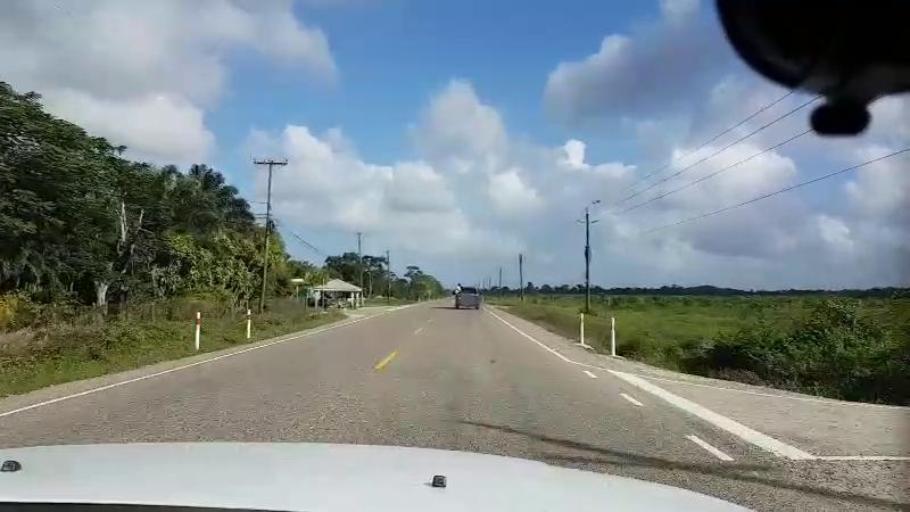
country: BZ
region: Stann Creek
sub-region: Dangriga
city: Dangriga
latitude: 16.9977
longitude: -88.3469
